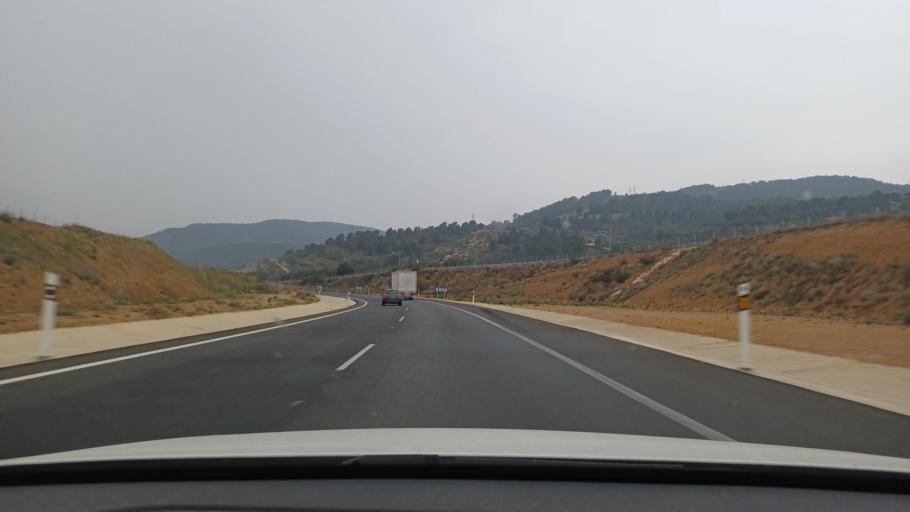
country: ES
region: Valencia
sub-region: Provincia de Valencia
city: La Font de la Figuera
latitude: 38.8306
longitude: -0.8866
